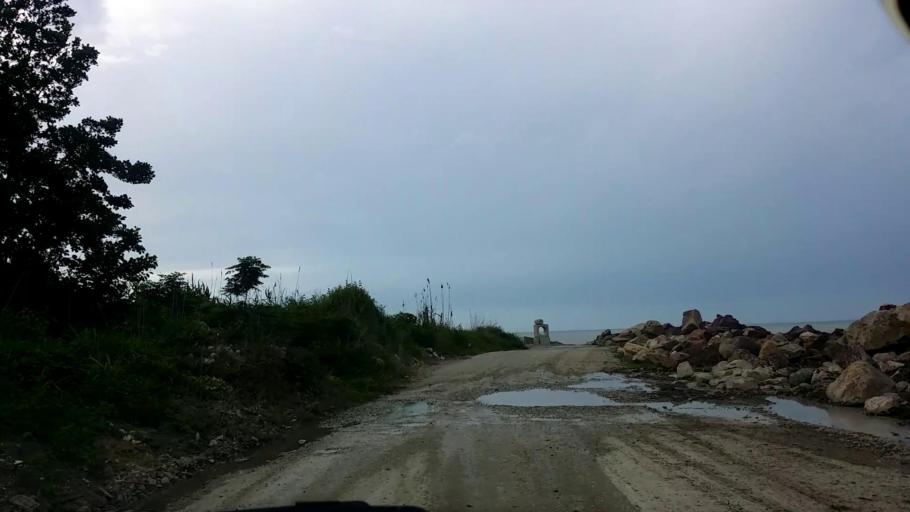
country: IR
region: Mazandaran
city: Chalus
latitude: 36.6847
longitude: 51.4289
